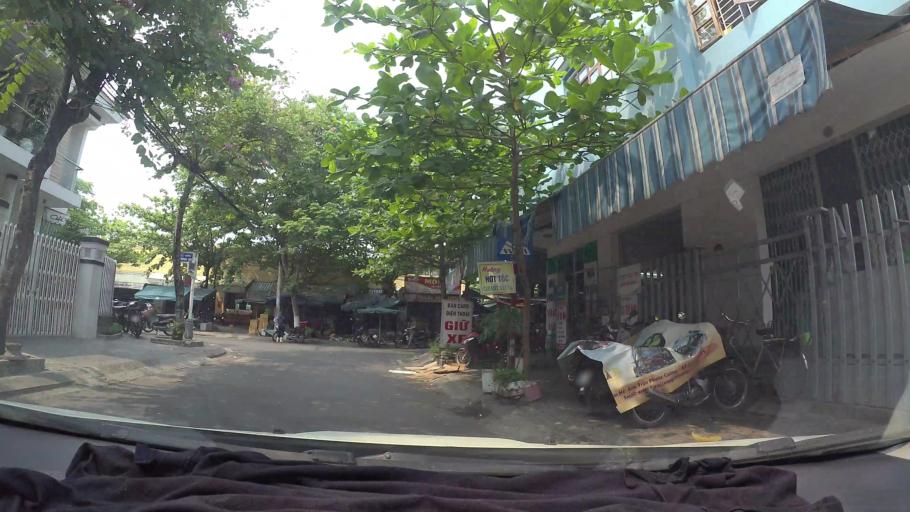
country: VN
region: Da Nang
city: Son Tra
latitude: 16.0428
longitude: 108.2182
